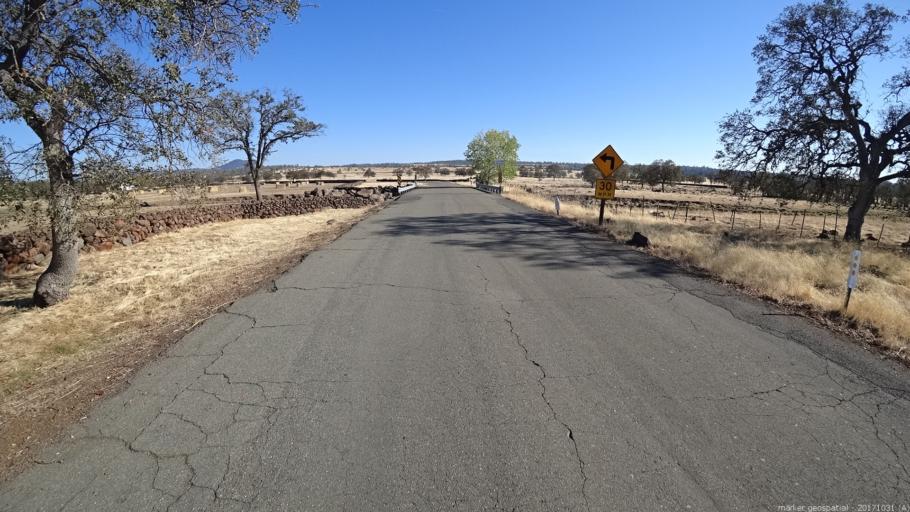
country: US
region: California
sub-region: Shasta County
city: Palo Cedro
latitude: 40.4629
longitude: -122.0943
